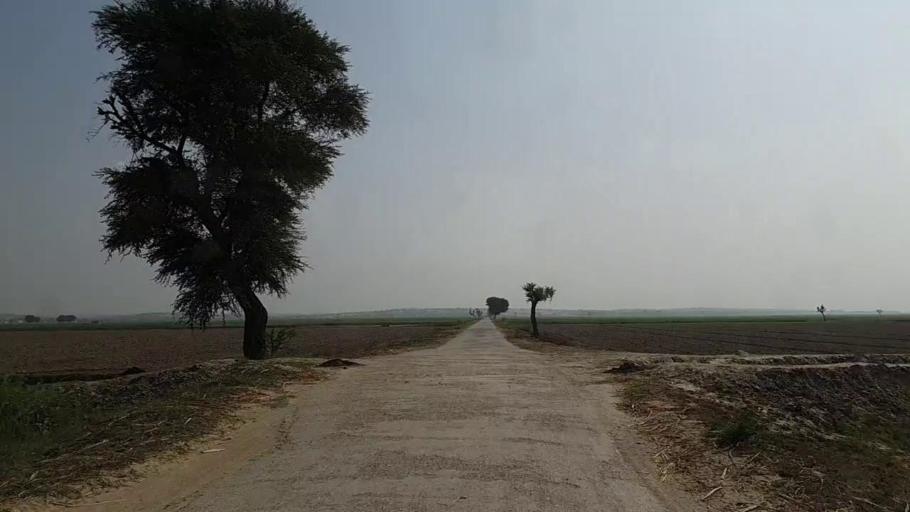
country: PK
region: Sindh
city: Naukot
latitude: 24.7606
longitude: 69.3473
